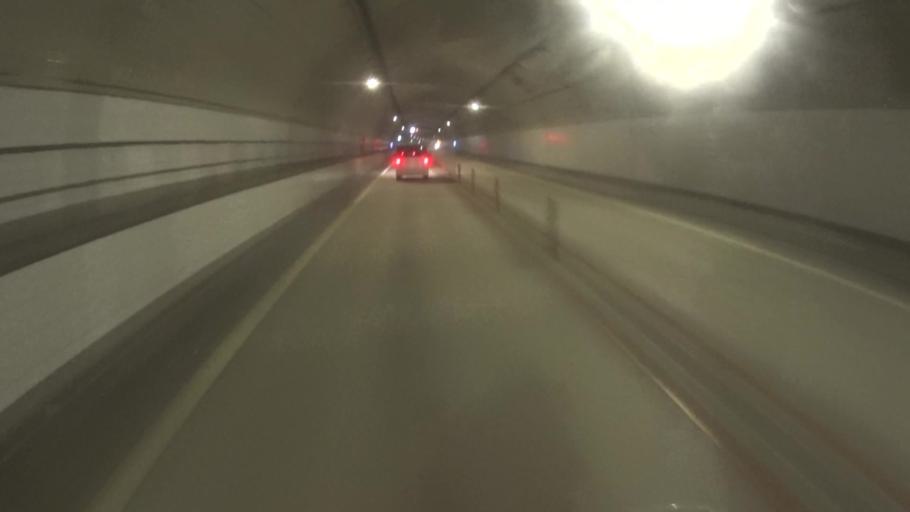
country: JP
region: Kyoto
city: Miyazu
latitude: 35.5382
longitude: 135.1598
